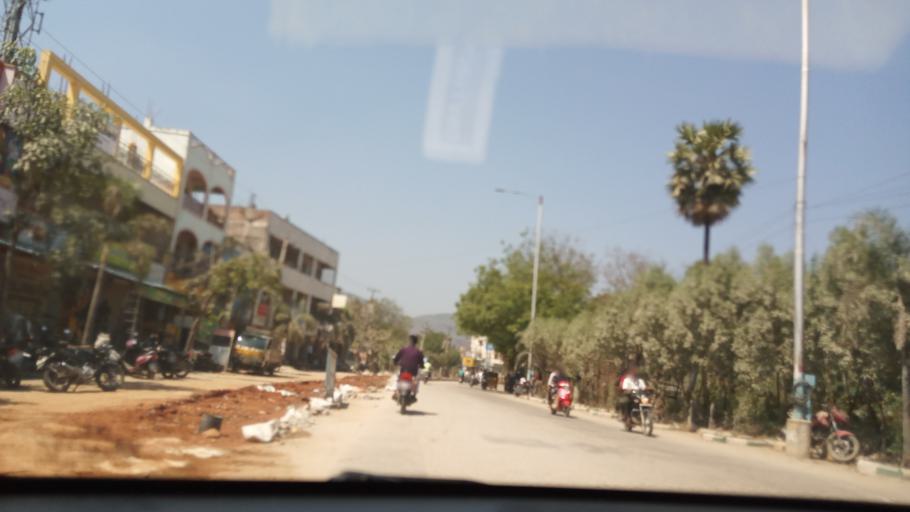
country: IN
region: Andhra Pradesh
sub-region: Chittoor
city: Tirupati
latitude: 13.6162
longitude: 79.4170
